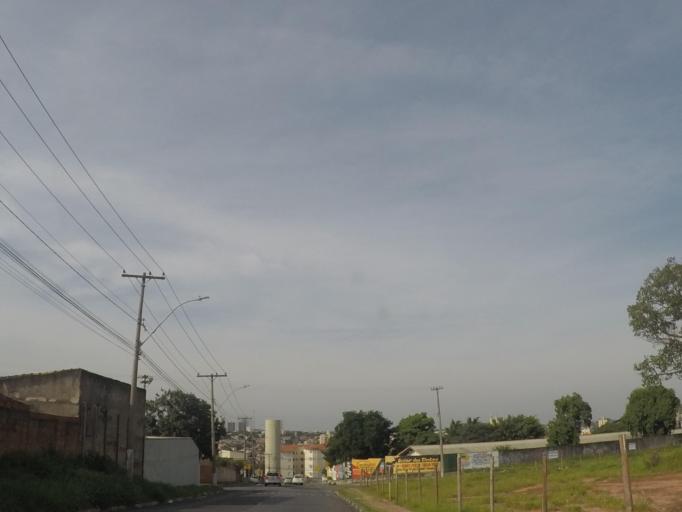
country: BR
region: Sao Paulo
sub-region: Hortolandia
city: Hortolandia
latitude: -22.8630
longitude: -47.2013
